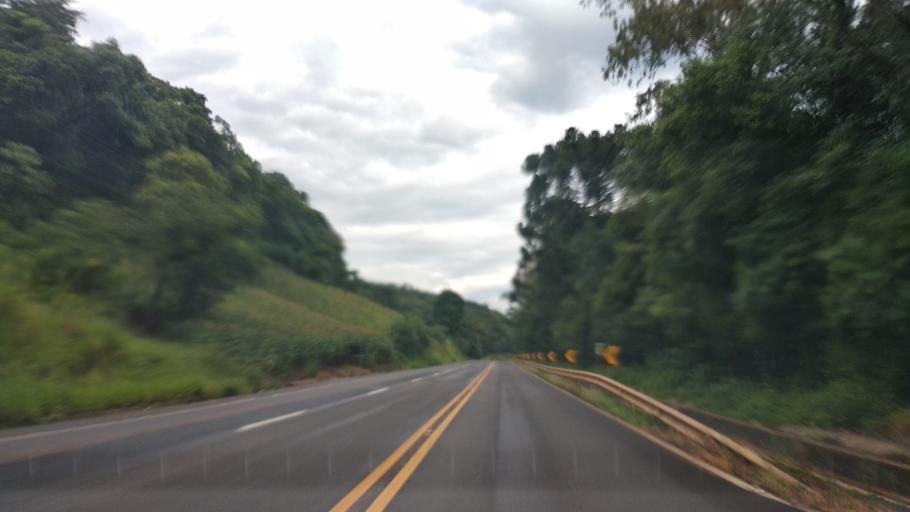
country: BR
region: Santa Catarina
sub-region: Videira
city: Videira
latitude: -27.0862
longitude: -51.2409
